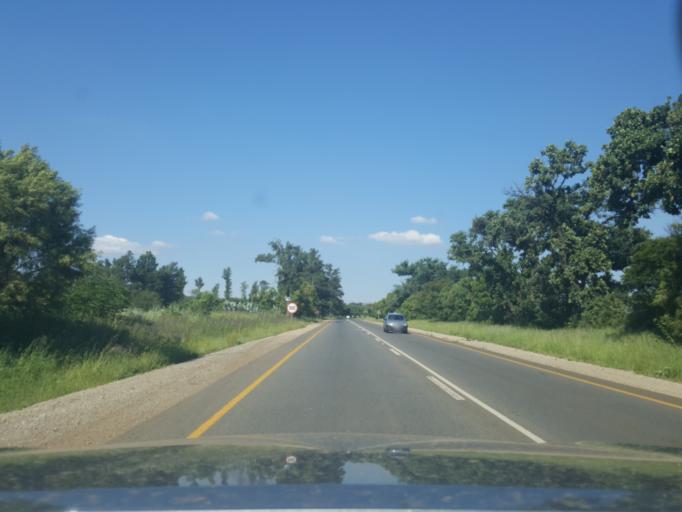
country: ZA
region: Gauteng
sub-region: City of Tshwane Metropolitan Municipality
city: Cullinan
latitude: -25.7538
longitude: 28.3856
